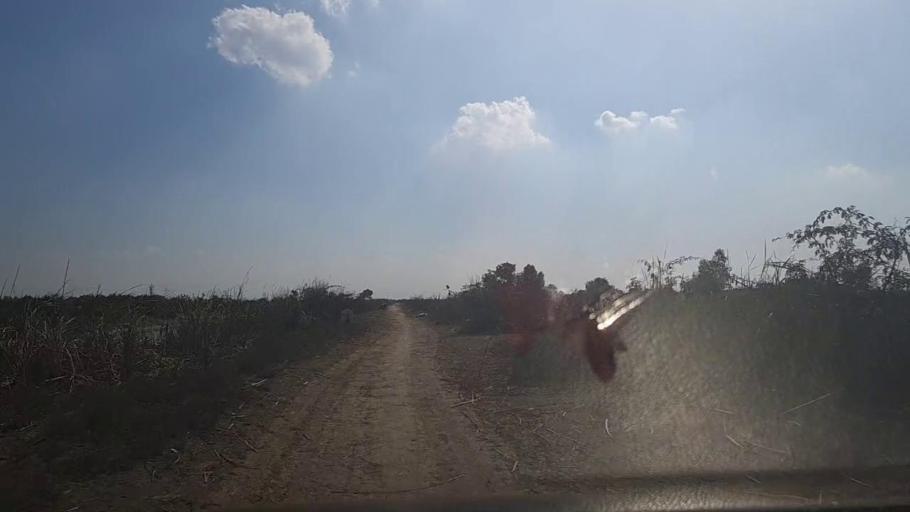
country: PK
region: Sindh
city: Tando Mittha Khan
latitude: 25.7994
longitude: 69.0731
